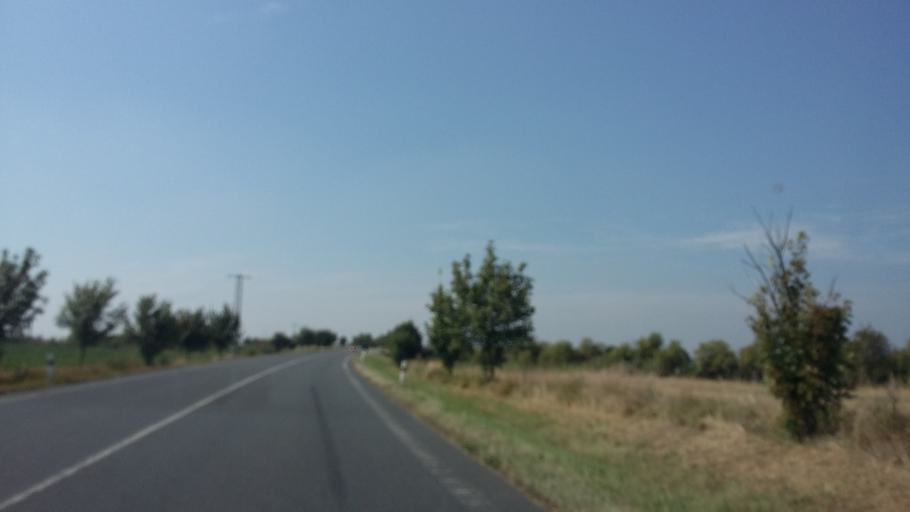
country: CZ
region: Central Bohemia
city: Velky Osek
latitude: 50.0955
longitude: 15.2610
